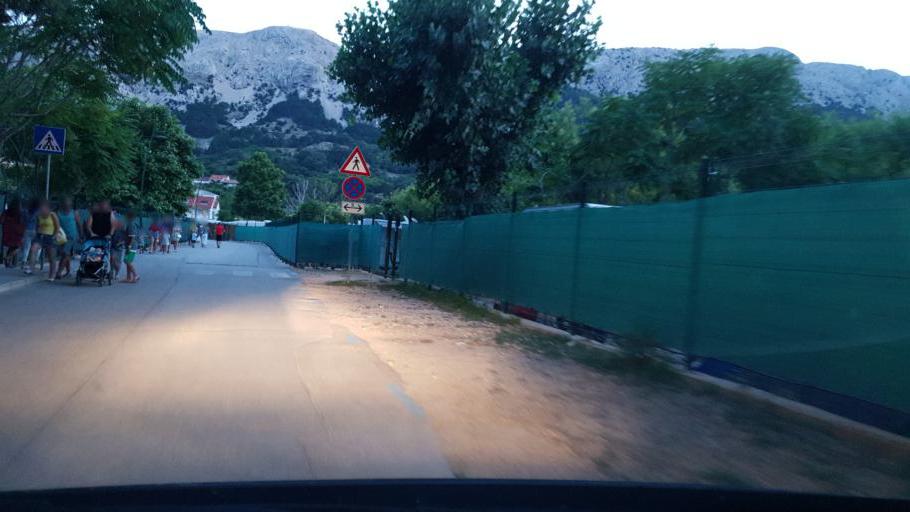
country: HR
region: Primorsko-Goranska
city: Punat
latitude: 44.9650
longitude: 14.7469
